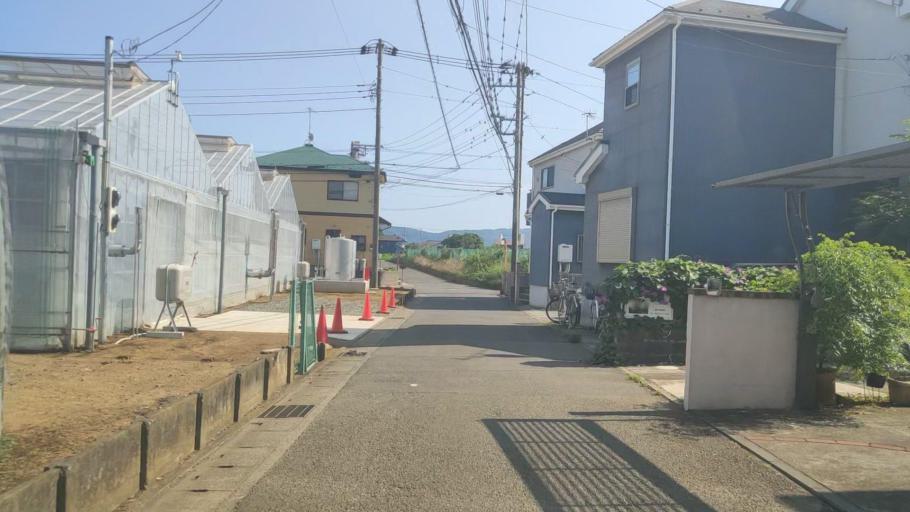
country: JP
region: Kanagawa
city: Hiratsuka
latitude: 35.3529
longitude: 139.3237
